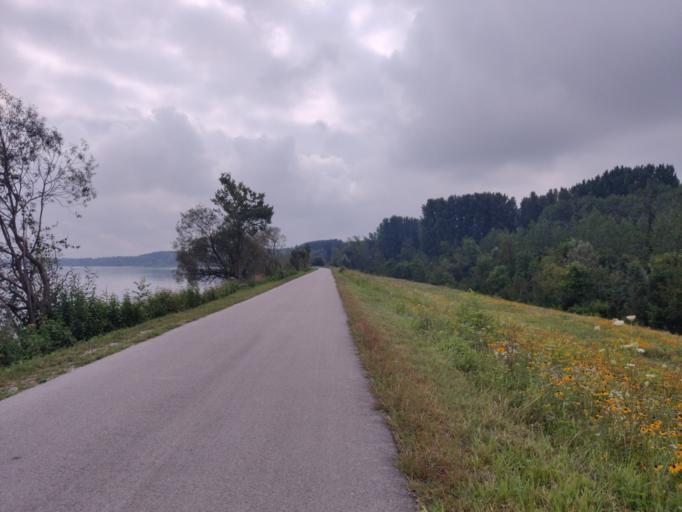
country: AT
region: Lower Austria
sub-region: Politischer Bezirk Sankt Polten
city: Traismauer
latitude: 48.3743
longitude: 15.7345
